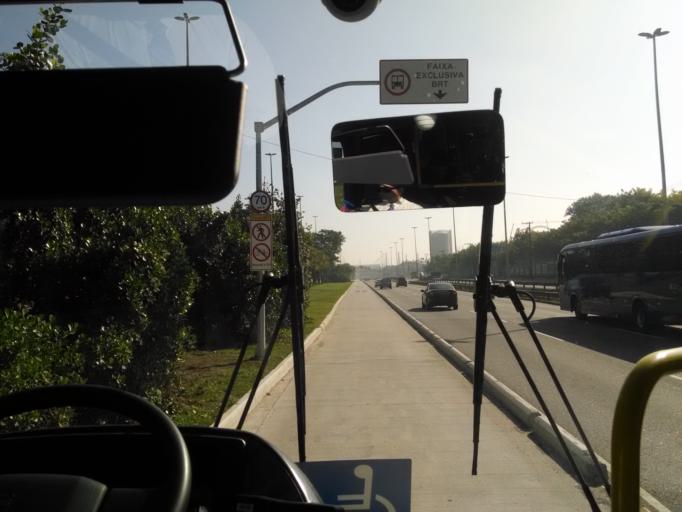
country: BR
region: Rio de Janeiro
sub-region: Rio De Janeiro
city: Rio de Janeiro
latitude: -22.9880
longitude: -43.3656
